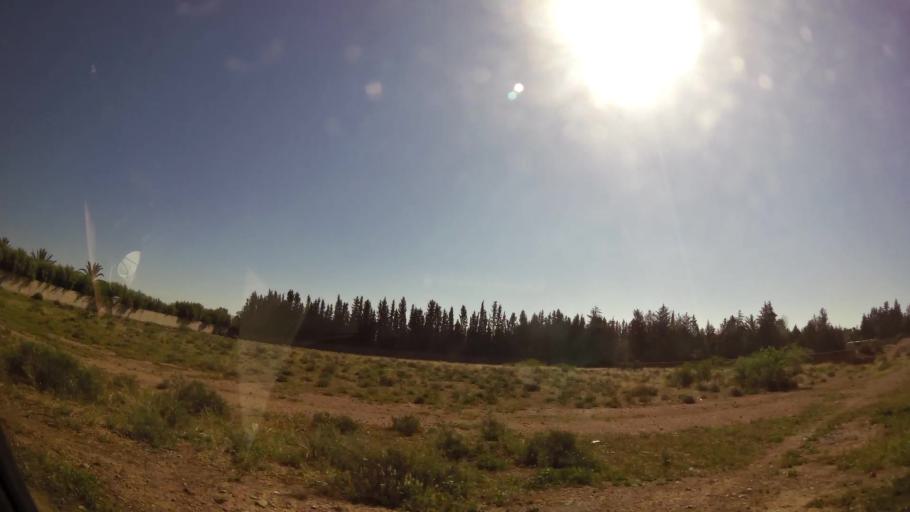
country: MA
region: Marrakech-Tensift-Al Haouz
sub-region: Marrakech
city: Marrakesh
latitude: 31.6644
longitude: -7.9403
